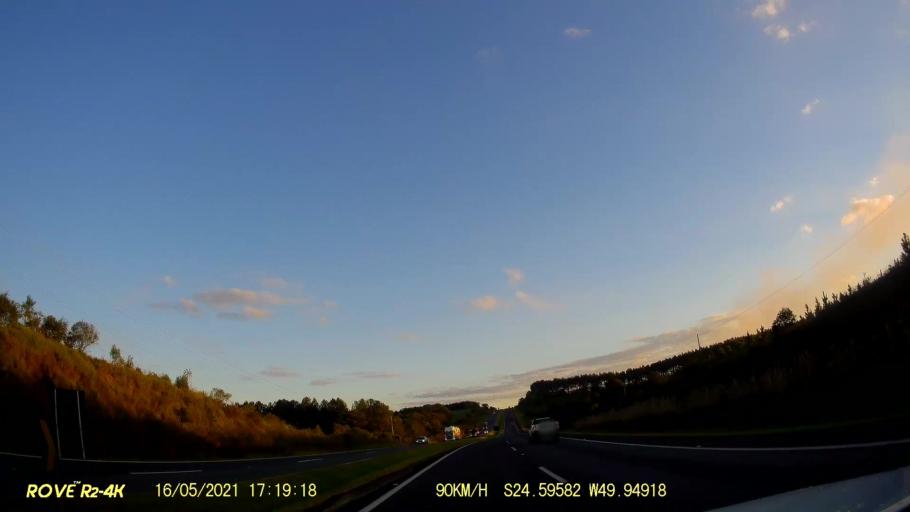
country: BR
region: Parana
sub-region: Pirai Do Sul
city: Pirai do Sul
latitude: -24.5962
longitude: -49.9493
